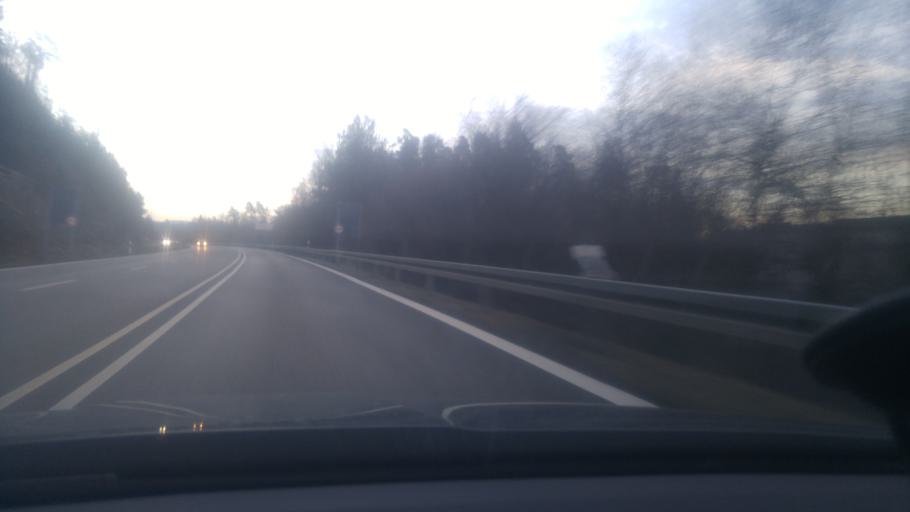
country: DE
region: Baden-Wuerttemberg
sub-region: Freiburg Region
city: Lauchringen
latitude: 47.6340
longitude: 8.3204
